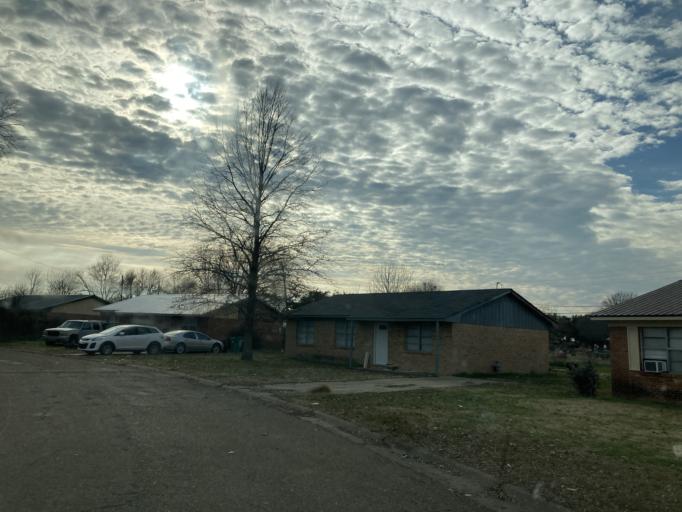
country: US
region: Mississippi
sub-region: Humphreys County
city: Belzoni
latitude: 33.1724
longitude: -90.5009
